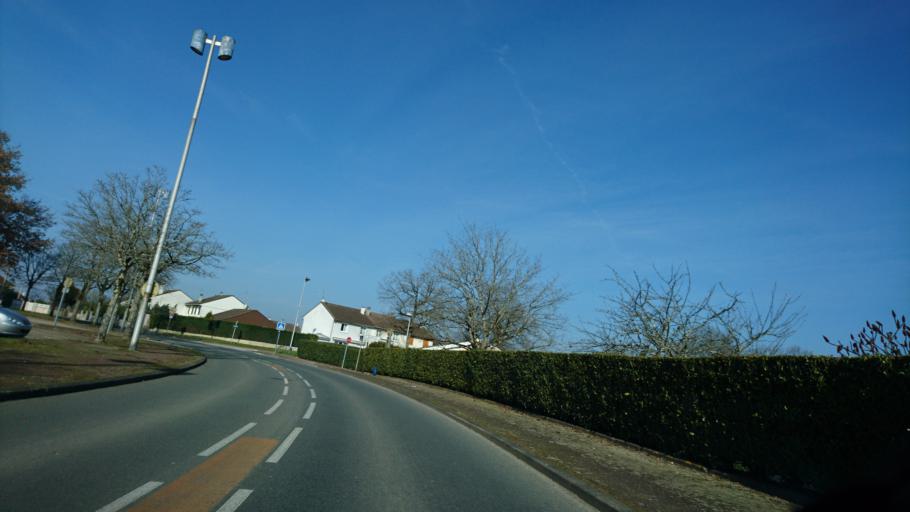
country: FR
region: Limousin
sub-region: Departement de la Haute-Vienne
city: Rilhac-Rancon
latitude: 45.8851
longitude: 1.2955
